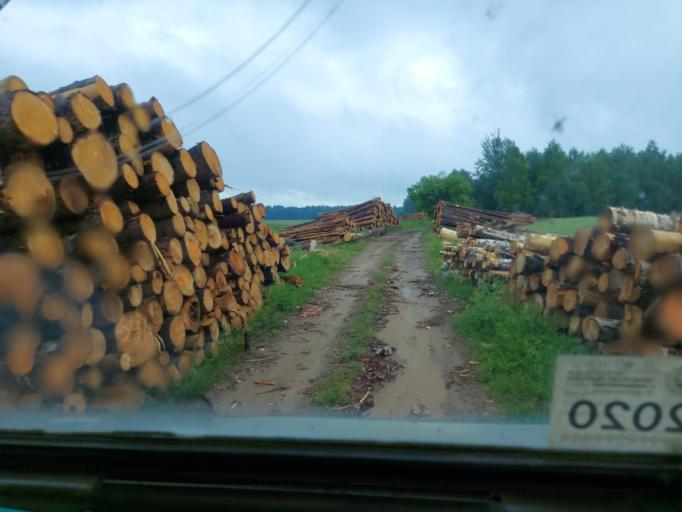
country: BY
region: Mogilev
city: Poselok Voskhod
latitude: 53.6742
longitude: 30.4005
